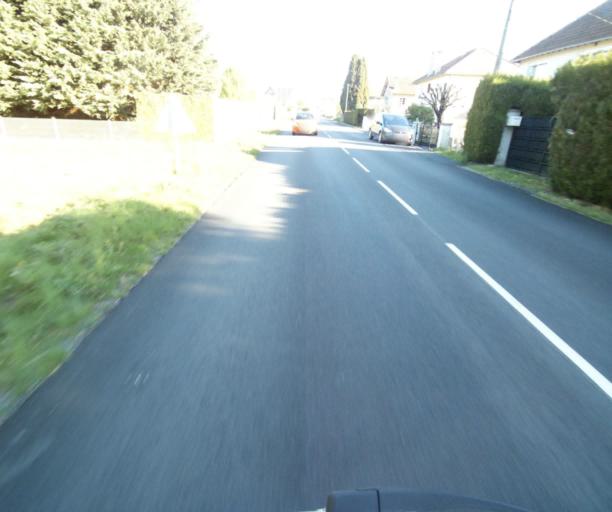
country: FR
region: Limousin
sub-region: Departement de la Correze
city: Correze
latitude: 45.3393
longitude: 1.8752
